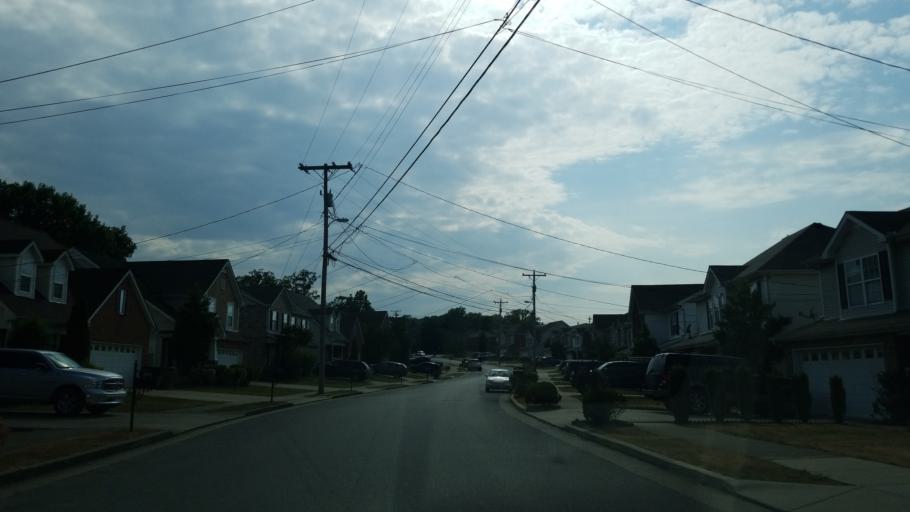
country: US
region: Tennessee
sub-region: Rutherford County
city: La Vergne
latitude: 36.0530
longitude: -86.5962
